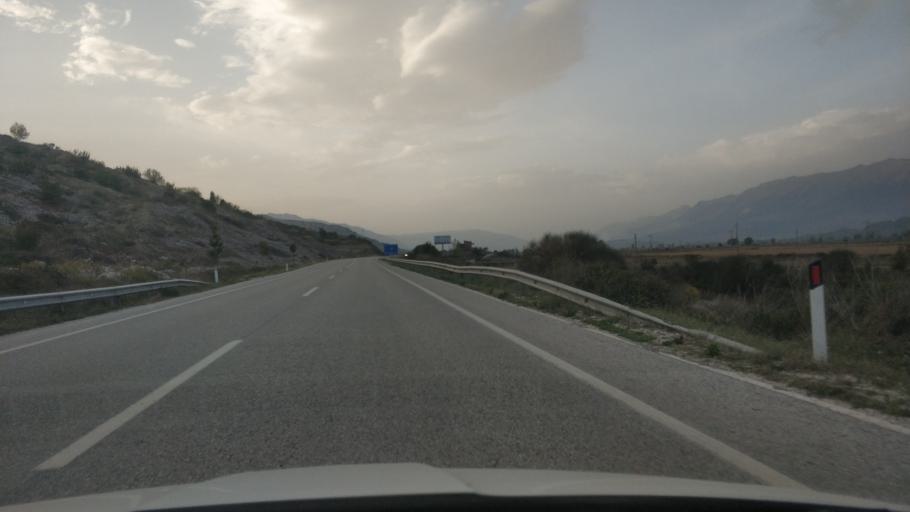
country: AL
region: Gjirokaster
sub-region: Rrethi i Gjirokastres
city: Libohove
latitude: 39.9463
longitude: 20.2602
